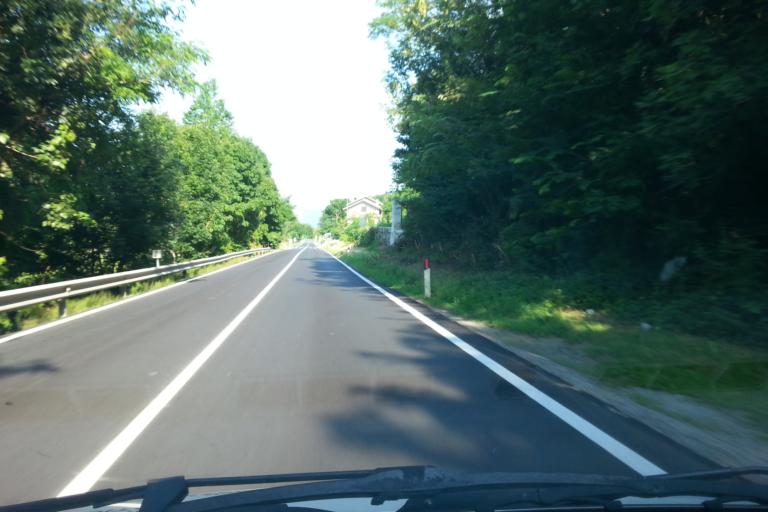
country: IT
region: Piedmont
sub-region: Provincia di Torino
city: San Didero
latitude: 45.1211
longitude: 7.2026
